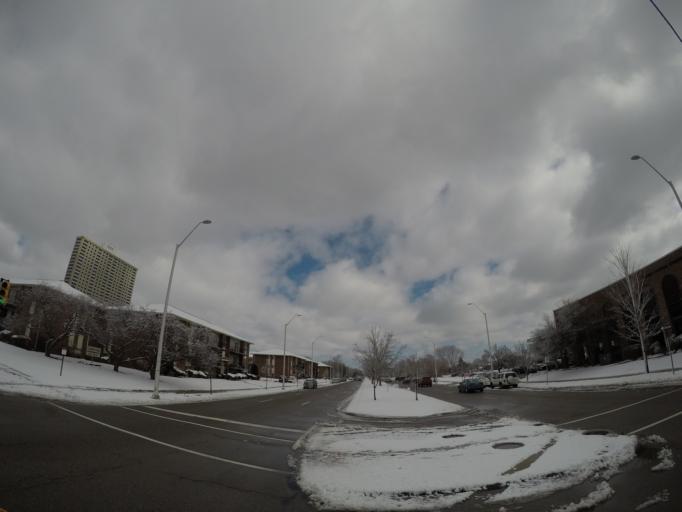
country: US
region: Michigan
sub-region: Wayne County
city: Detroit
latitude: 42.3341
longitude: -83.0347
